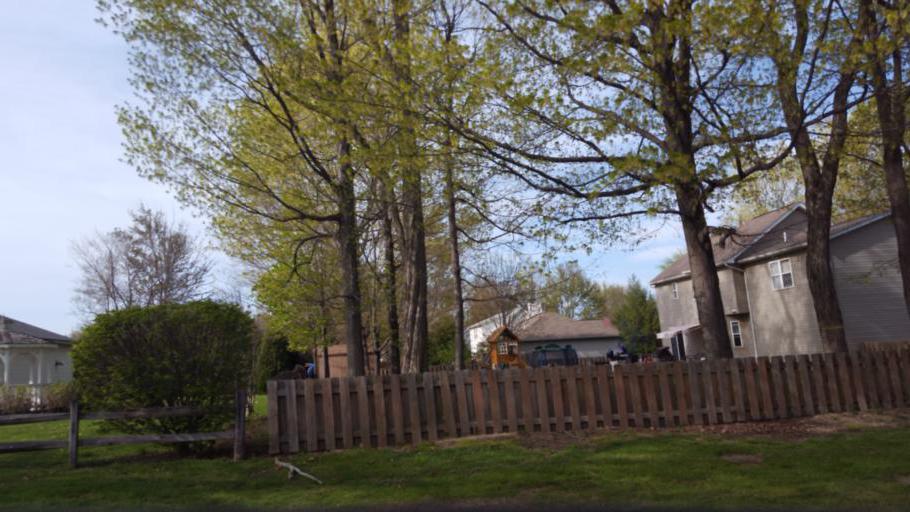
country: US
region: Ohio
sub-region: Lake County
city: North Madison
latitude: 41.8419
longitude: -81.0094
